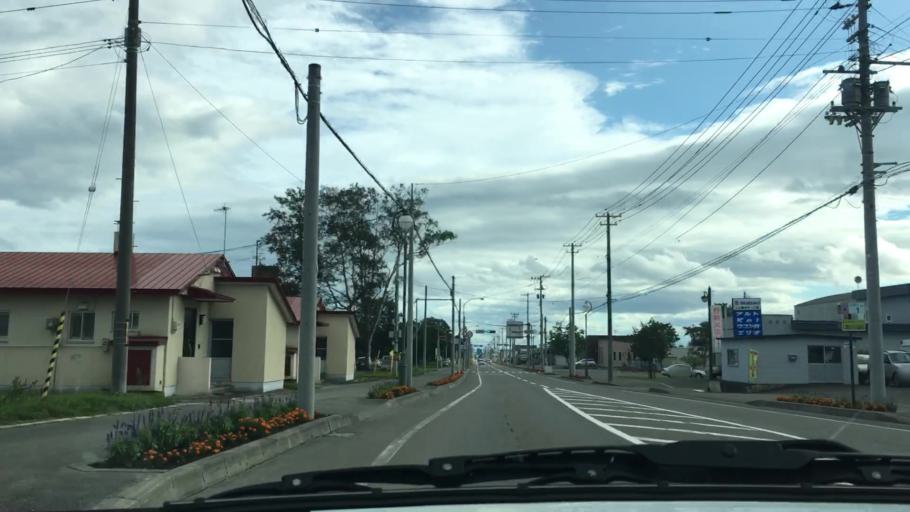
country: JP
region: Hokkaido
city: Otofuke
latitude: 43.2341
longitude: 143.2954
